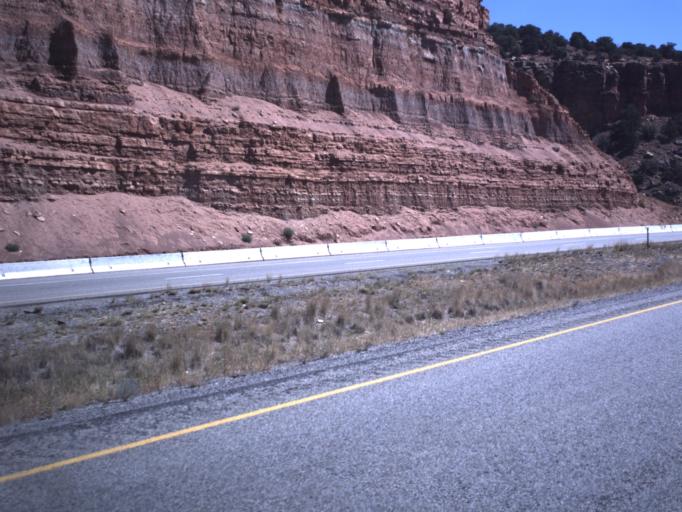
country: US
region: Utah
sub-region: Sevier County
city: Salina
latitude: 38.9317
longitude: -111.7889
